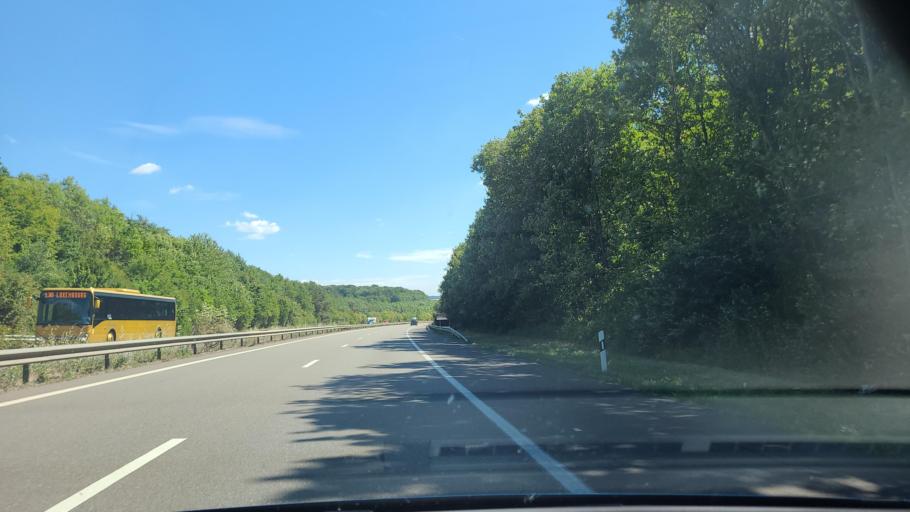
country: LU
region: Grevenmacher
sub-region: Canton de Grevenmacher
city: Manternach
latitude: 49.6832
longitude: 6.4076
